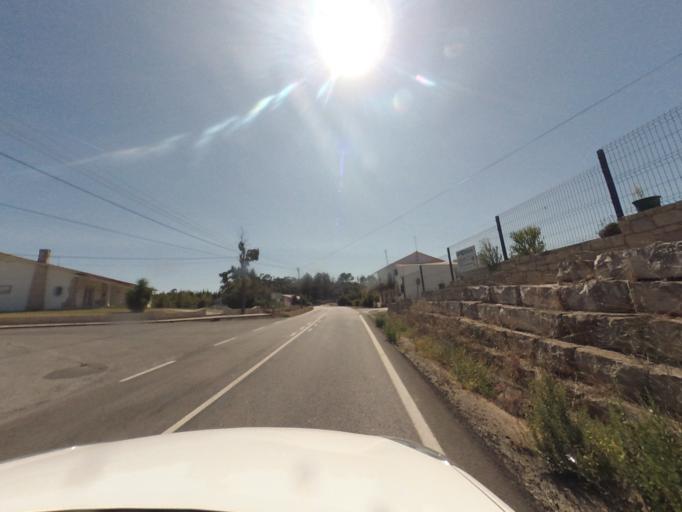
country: PT
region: Leiria
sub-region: Alcobaca
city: Alcobaca
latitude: 39.5296
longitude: -8.9637
